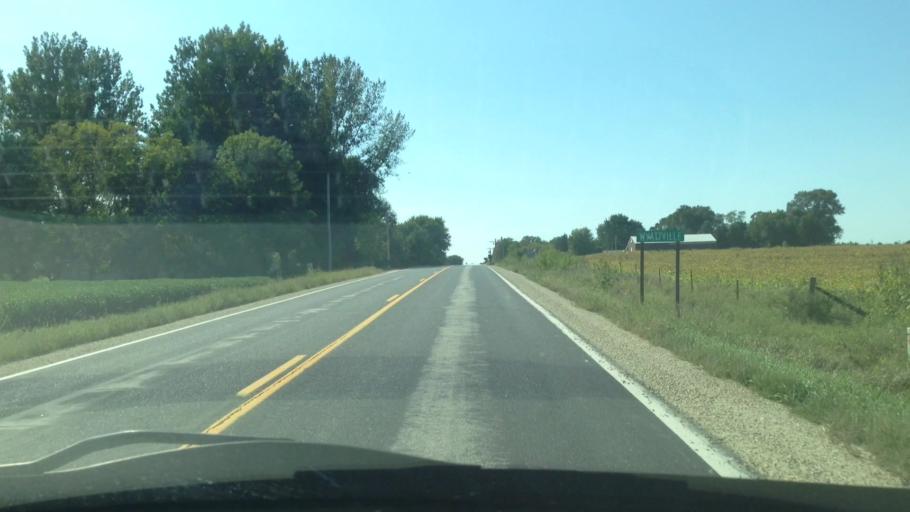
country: US
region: Minnesota
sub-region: Winona County
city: Lewiston
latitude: 43.9404
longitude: -91.7859
